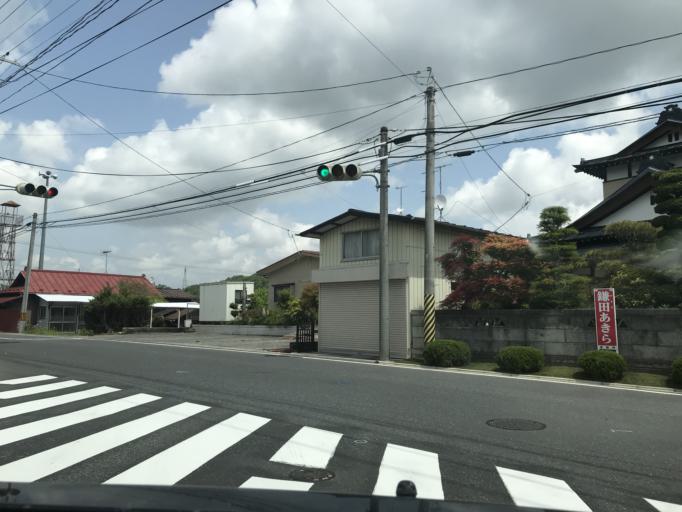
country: JP
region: Miyagi
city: Kogota
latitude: 38.6623
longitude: 141.0668
